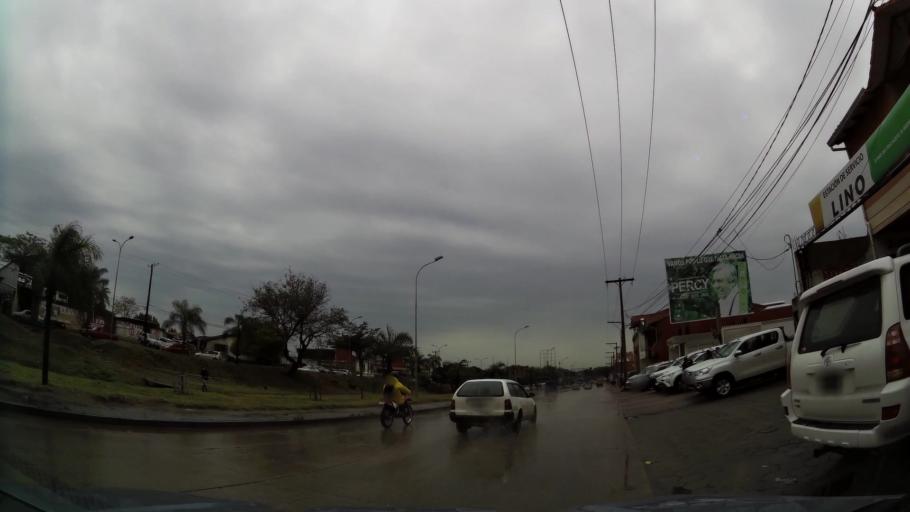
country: BO
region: Santa Cruz
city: Santa Cruz de la Sierra
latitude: -17.8174
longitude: -63.2010
